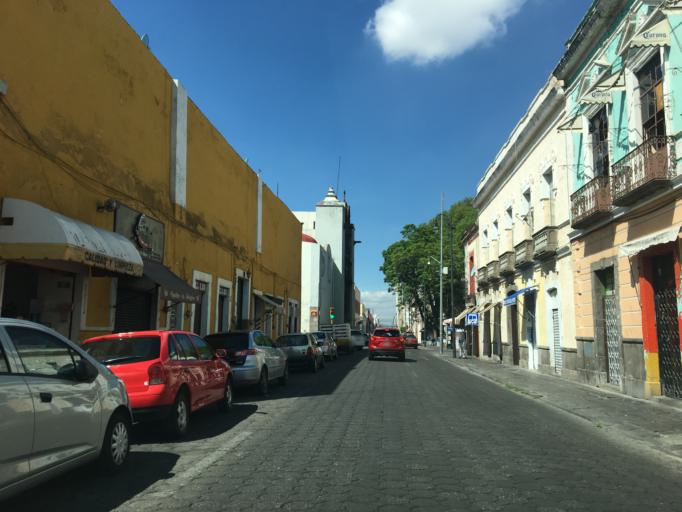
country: MX
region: Puebla
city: Puebla
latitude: 19.0426
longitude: -98.2017
